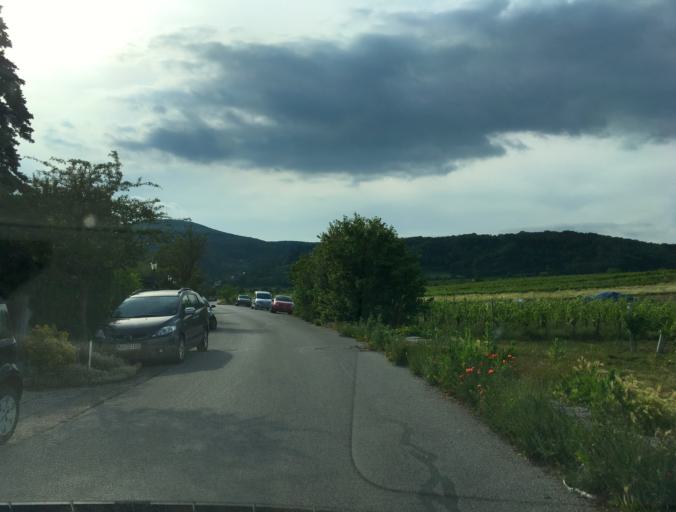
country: AT
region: Lower Austria
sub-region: Politischer Bezirk Modling
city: Gumpoldskirchen
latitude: 48.0459
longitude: 16.2868
